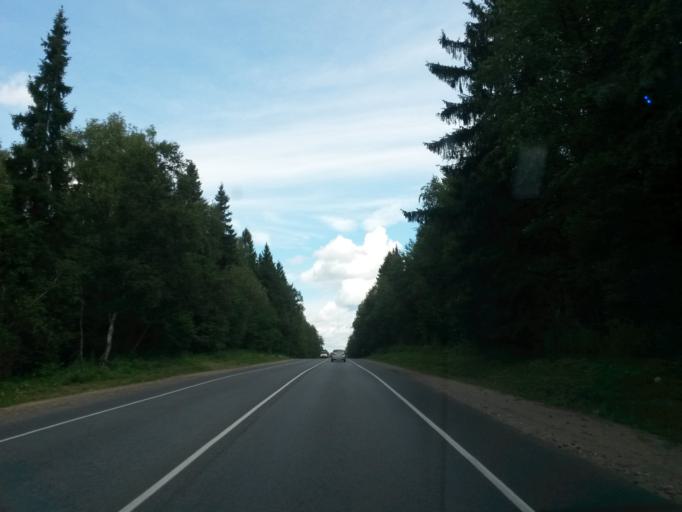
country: RU
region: Jaroslavl
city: Pereslavl'-Zalesskiy
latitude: 56.8054
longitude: 38.8963
